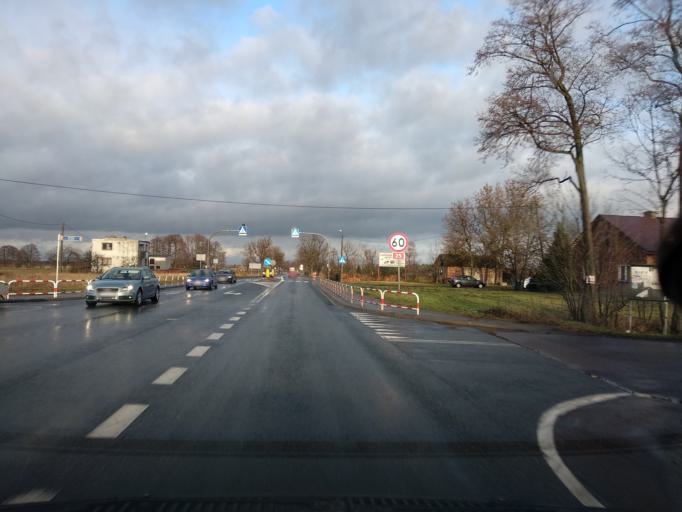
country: PL
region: Greater Poland Voivodeship
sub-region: Powiat koninski
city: Rychwal
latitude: 52.0953
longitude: 18.1664
